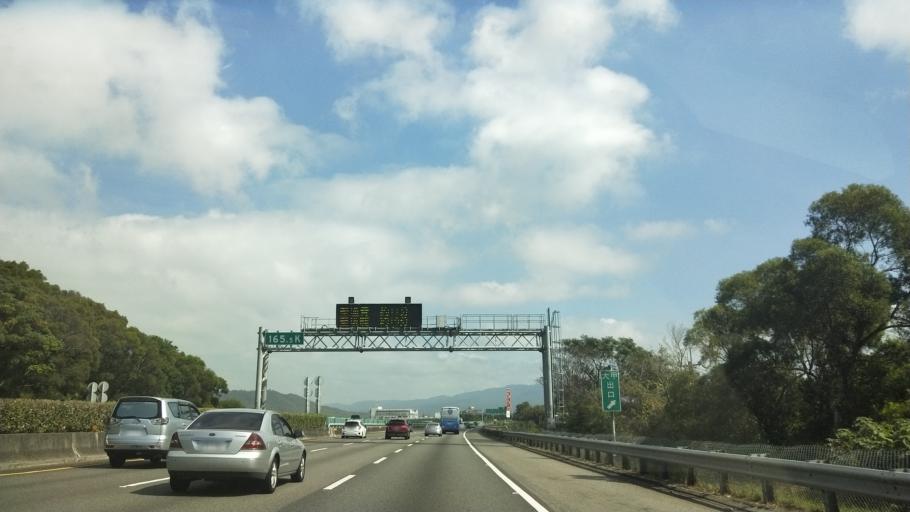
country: TW
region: Taiwan
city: Fengyuan
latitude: 24.3323
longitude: 120.6313
